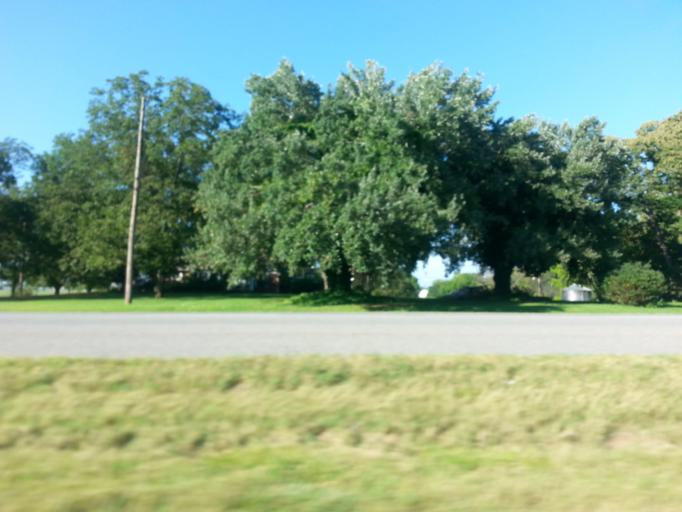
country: US
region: Alabama
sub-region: Colbert County
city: Muscle Shoals
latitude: 34.7130
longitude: -87.6720
